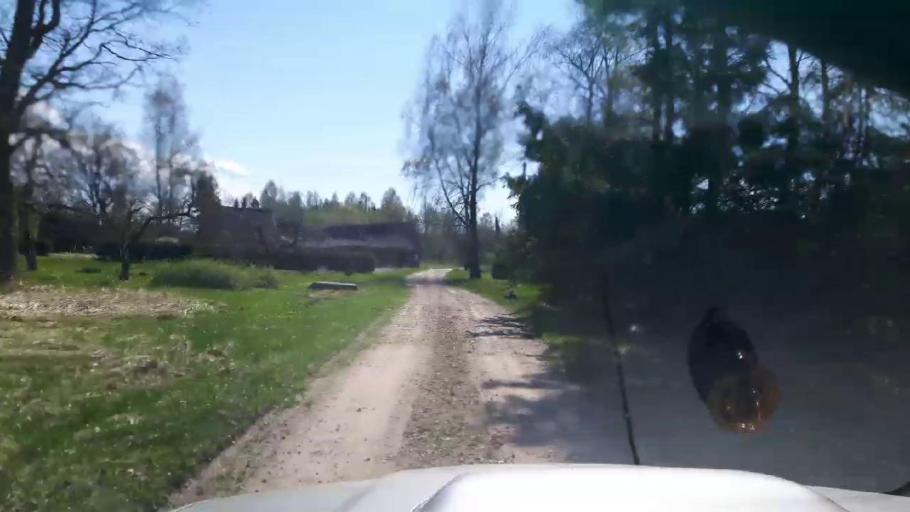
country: EE
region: Paernumaa
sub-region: Tootsi vald
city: Tootsi
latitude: 58.4629
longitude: 24.7980
